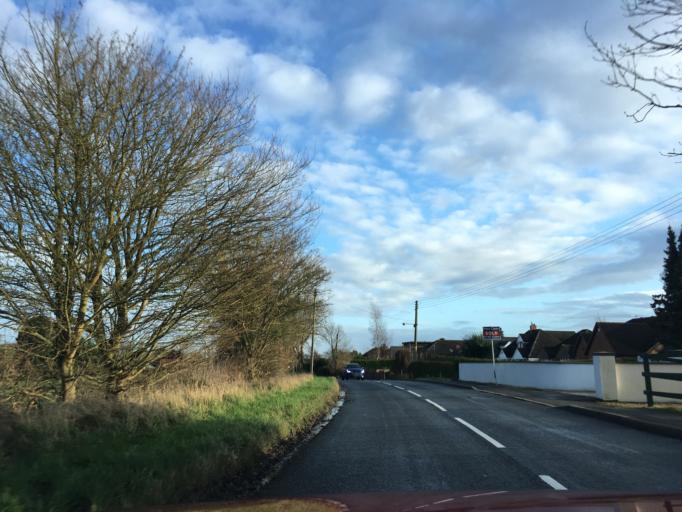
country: GB
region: England
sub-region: Warwickshire
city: Henley in Arden
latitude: 52.2239
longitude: -1.7732
